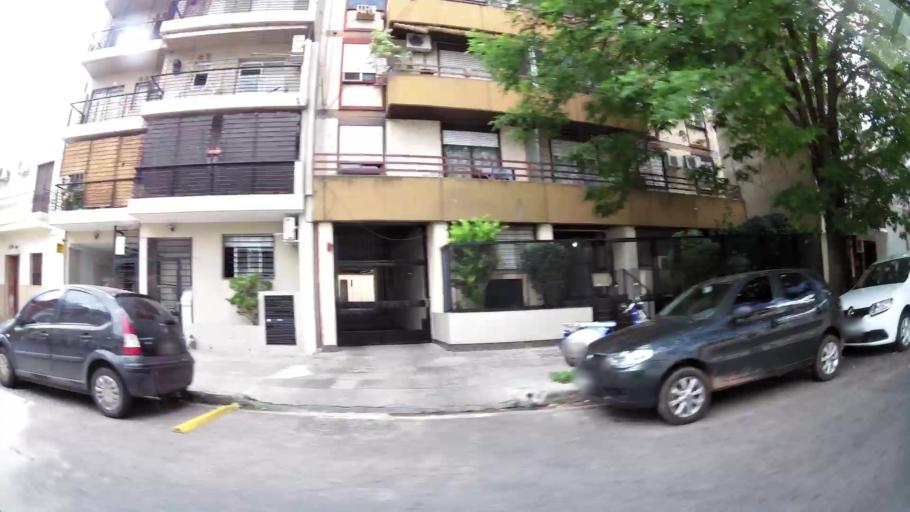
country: AR
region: Santa Fe
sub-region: Departamento de Rosario
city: Rosario
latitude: -32.9596
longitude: -60.6326
